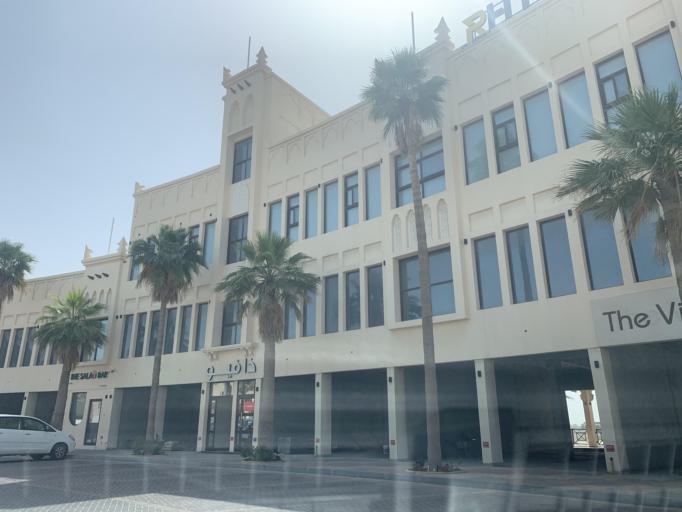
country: BH
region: Northern
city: Ar Rifa'
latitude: 26.1467
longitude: 50.5668
